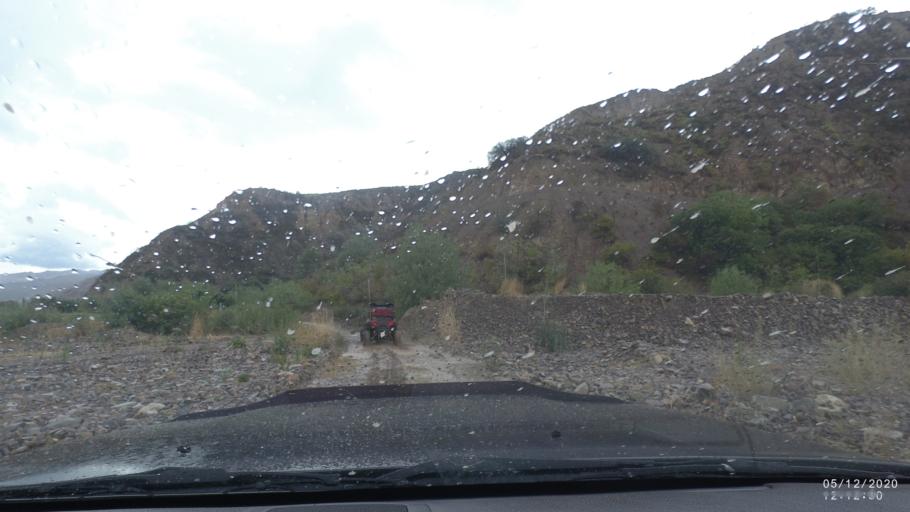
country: BO
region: Cochabamba
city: Sipe Sipe
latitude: -17.5626
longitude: -66.3772
